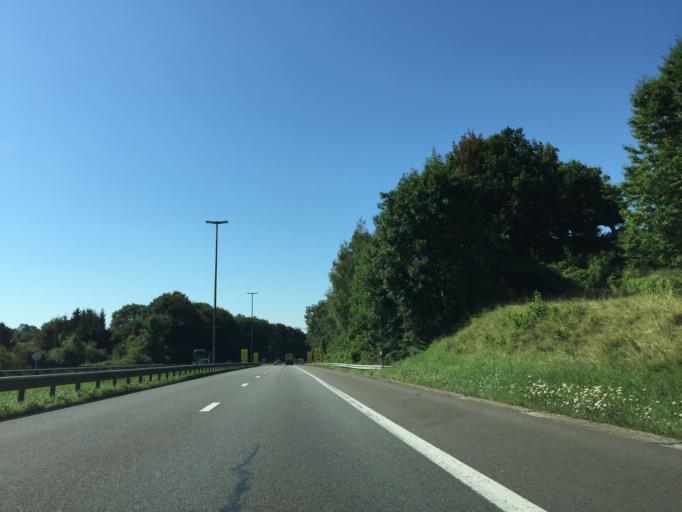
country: BE
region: Wallonia
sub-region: Province de Liege
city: Dison
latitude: 50.6177
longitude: 5.8536
